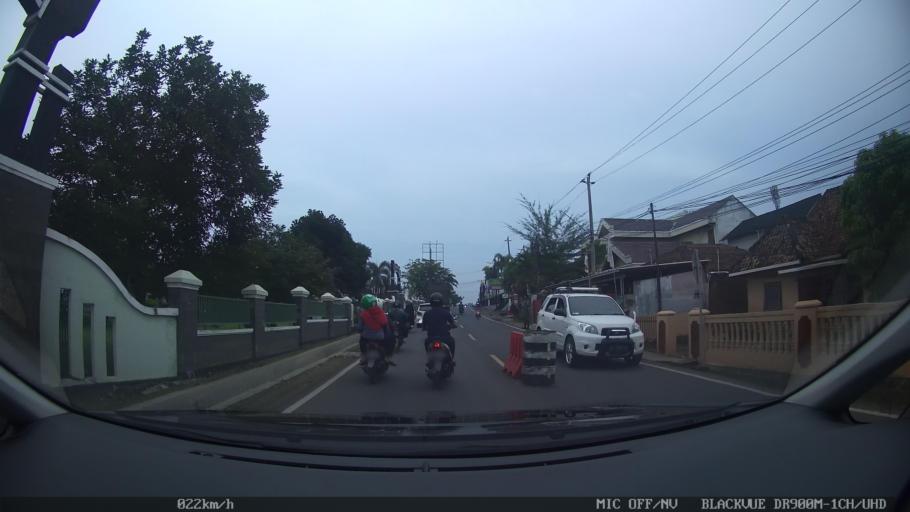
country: ID
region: Lampung
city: Kedaton
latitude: -5.3964
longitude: 105.2377
